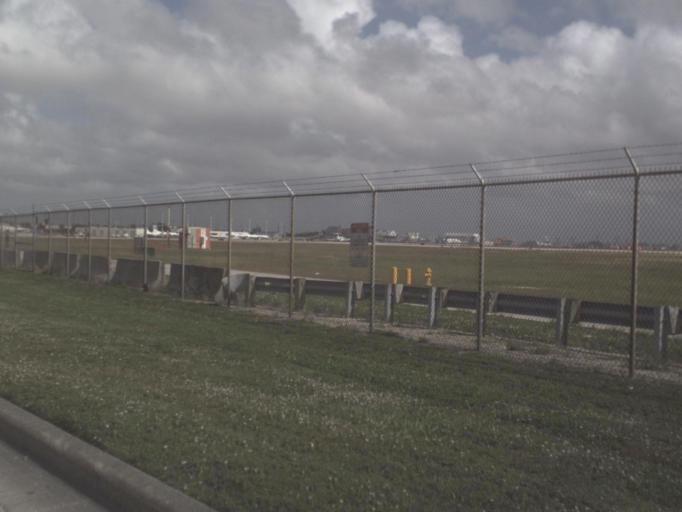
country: US
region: Florida
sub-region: Miami-Dade County
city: Virginia Gardens
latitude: 25.8015
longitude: -80.3057
